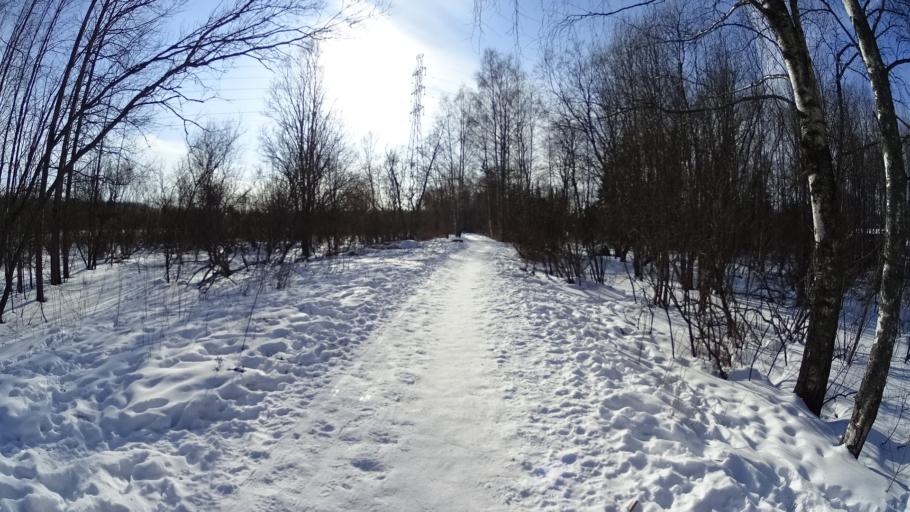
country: FI
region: Uusimaa
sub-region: Helsinki
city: Kauniainen
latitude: 60.2424
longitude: 24.7251
